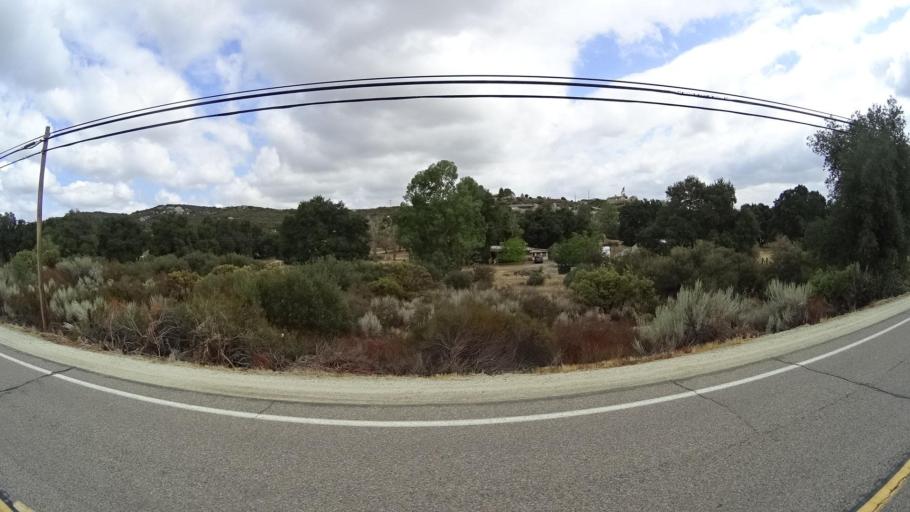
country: US
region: California
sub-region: San Diego County
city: Campo
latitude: 32.6476
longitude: -116.4873
